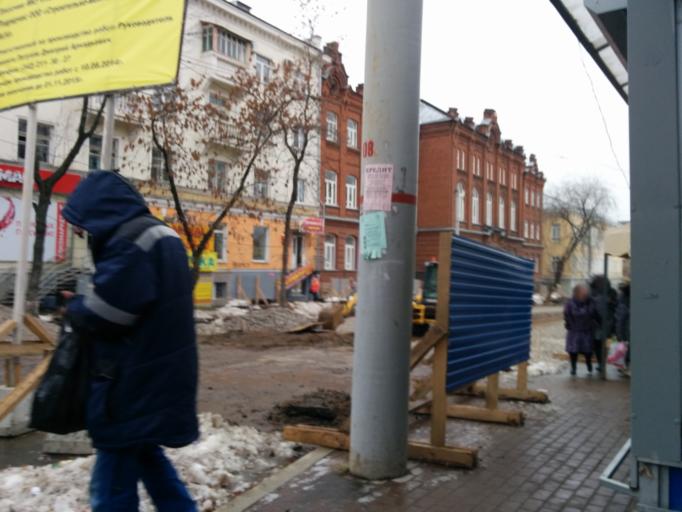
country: RU
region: Perm
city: Perm
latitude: 58.0154
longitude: 56.2526
